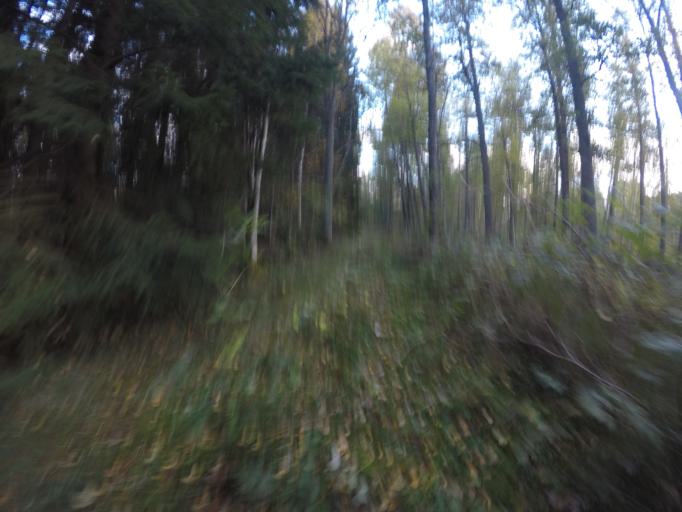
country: SE
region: Vaestmanland
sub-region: Arboga Kommun
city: Tyringe
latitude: 59.3336
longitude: 15.9665
